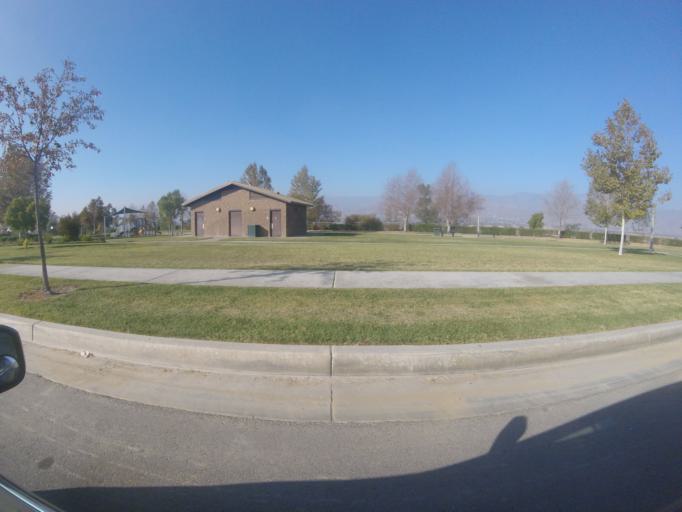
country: US
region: California
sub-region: San Bernardino County
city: Redlands
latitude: 34.0860
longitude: -117.1856
